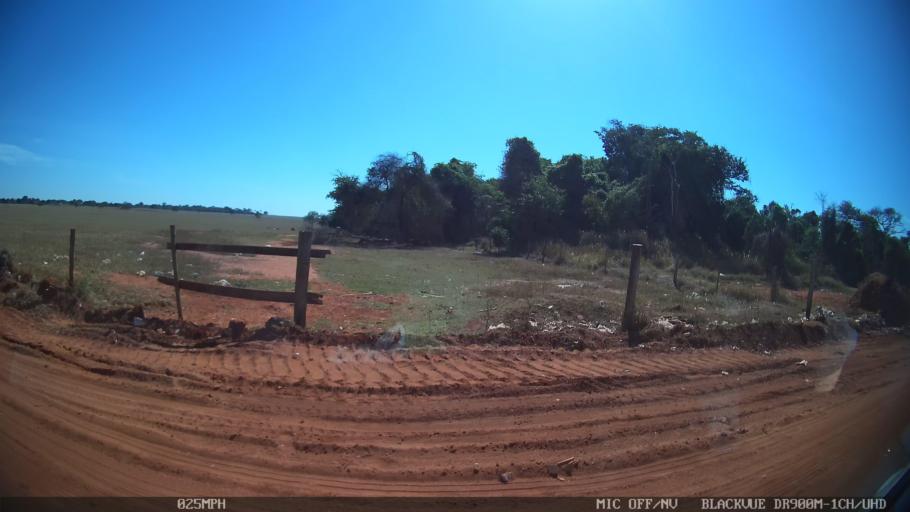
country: BR
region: Sao Paulo
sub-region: Sao Jose Do Rio Preto
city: Sao Jose do Rio Preto
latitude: -20.7411
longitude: -49.4221
